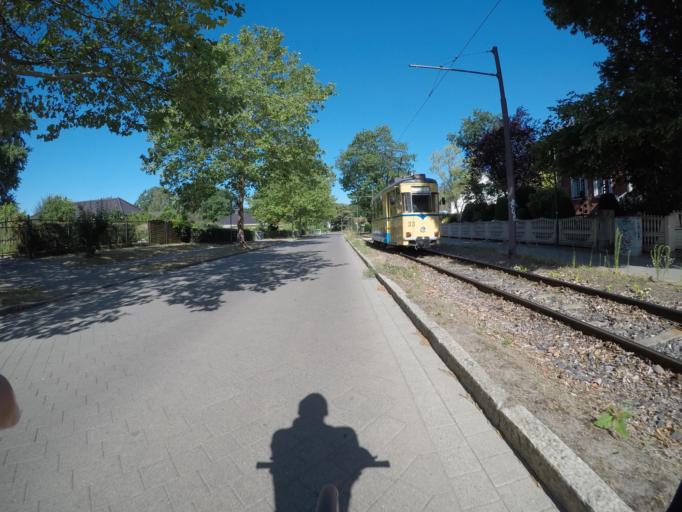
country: DE
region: Brandenburg
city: Woltersdorf
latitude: 52.4553
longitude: 13.7341
